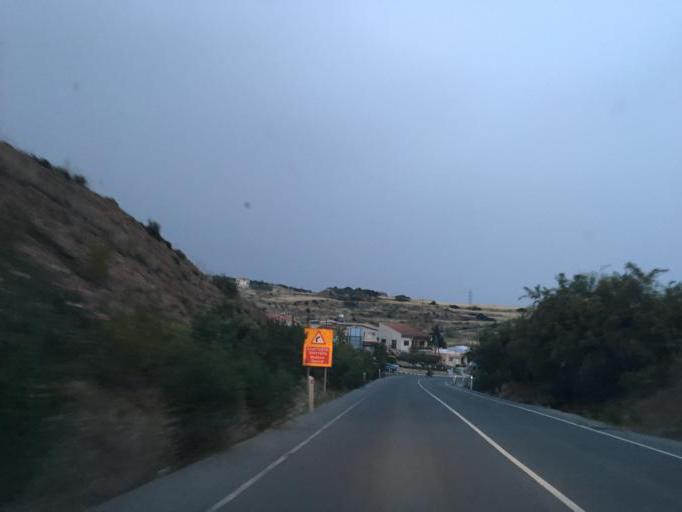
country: CY
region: Limassol
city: Parekklisha
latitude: 34.7389
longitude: 33.1602
